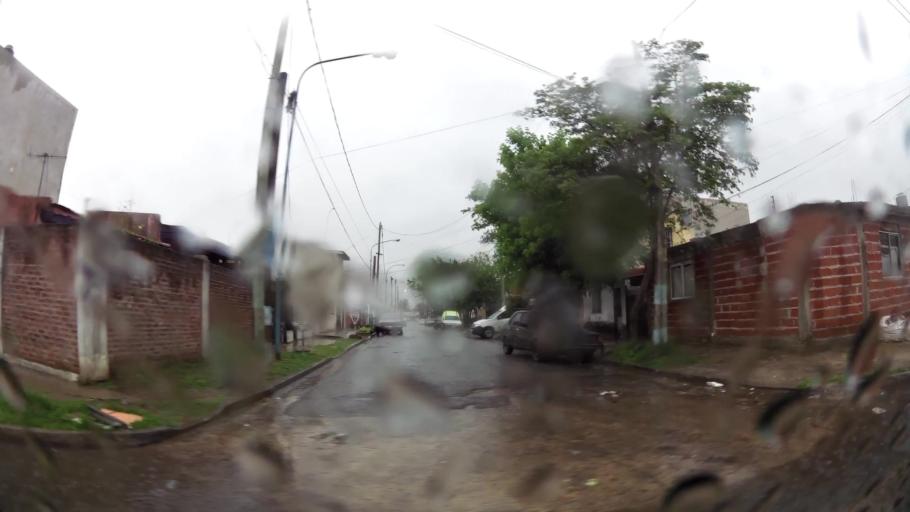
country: AR
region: Buenos Aires
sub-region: Partido de Lanus
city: Lanus
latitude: -34.7196
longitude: -58.4081
